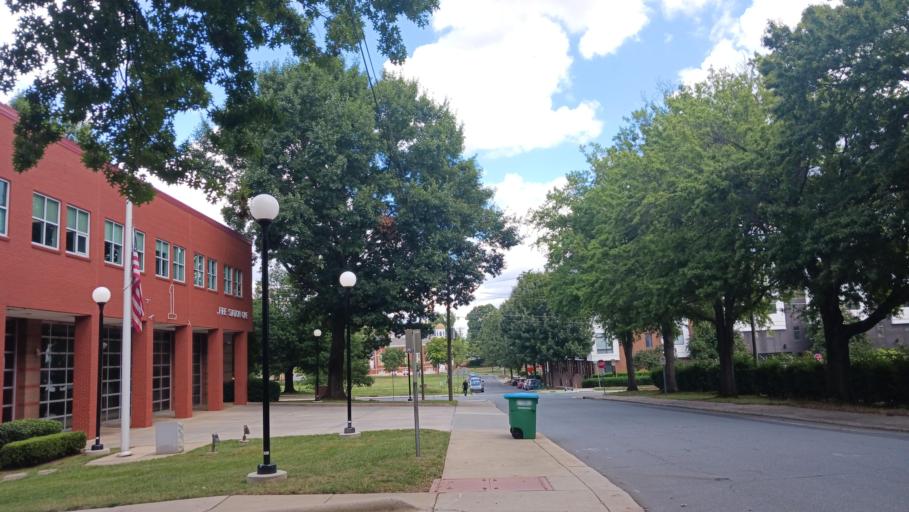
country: US
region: North Carolina
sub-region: Mecklenburg County
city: Charlotte
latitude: 35.2224
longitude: -80.8345
